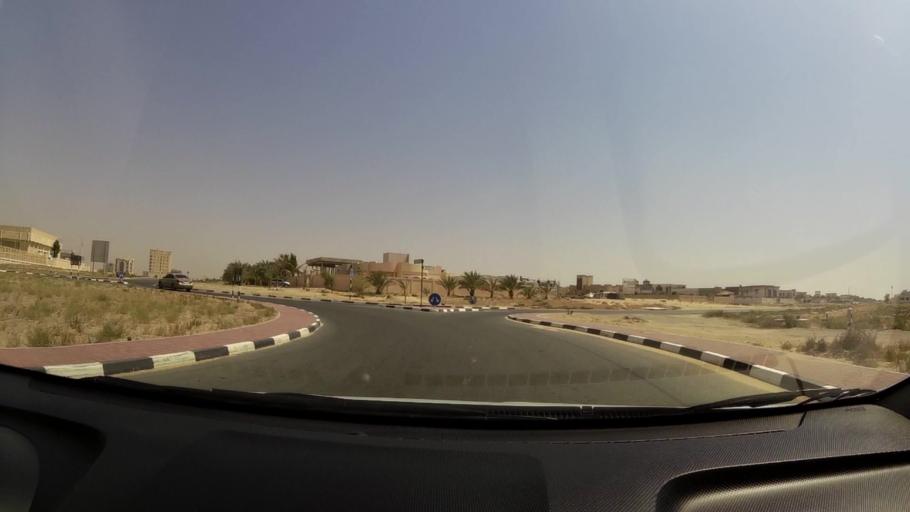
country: AE
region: Umm al Qaywayn
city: Umm al Qaywayn
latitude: 25.5003
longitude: 55.5966
